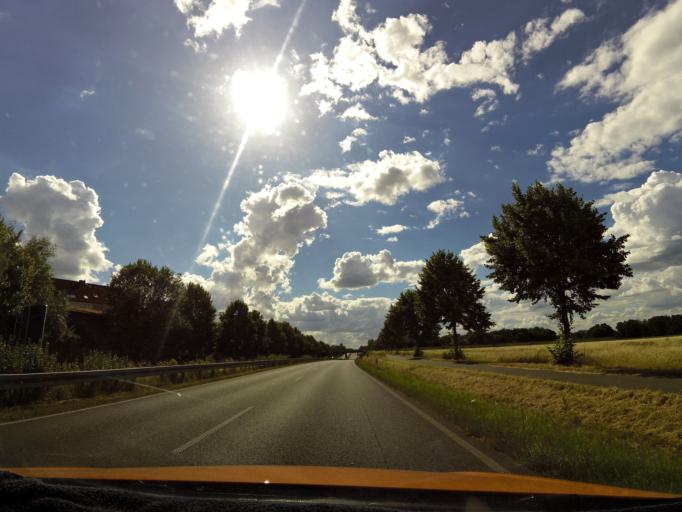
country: DE
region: Berlin
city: Lichtenrade
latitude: 52.3673
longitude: 13.4100
